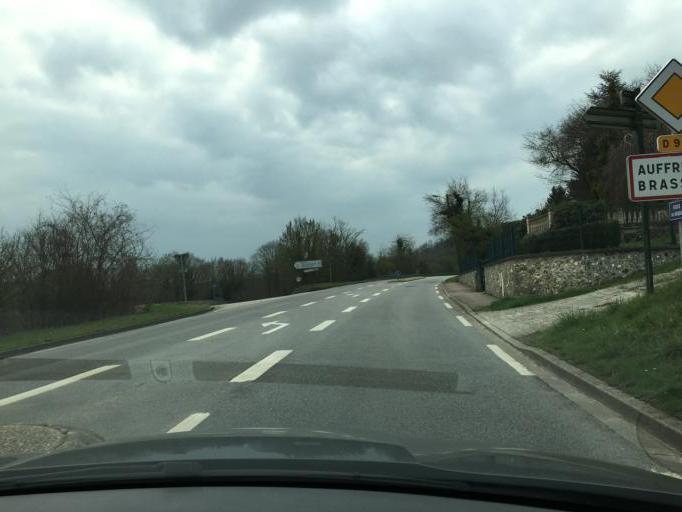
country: FR
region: Ile-de-France
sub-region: Departement des Yvelines
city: Mantes-la-Ville
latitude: 48.9533
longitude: 1.7046
